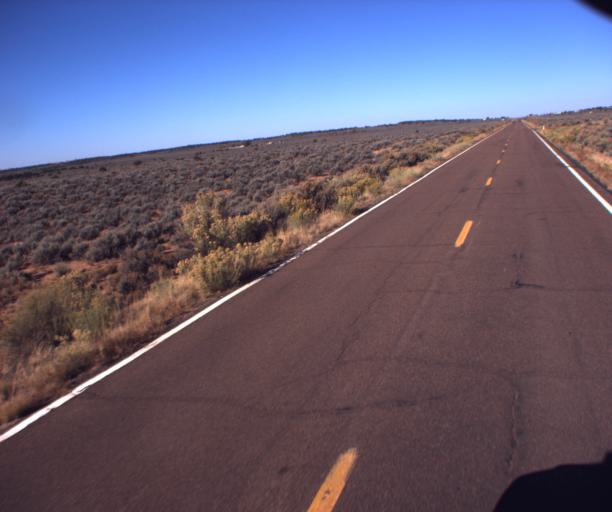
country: US
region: Arizona
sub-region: Apache County
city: Ganado
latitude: 35.7505
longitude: -109.9390
